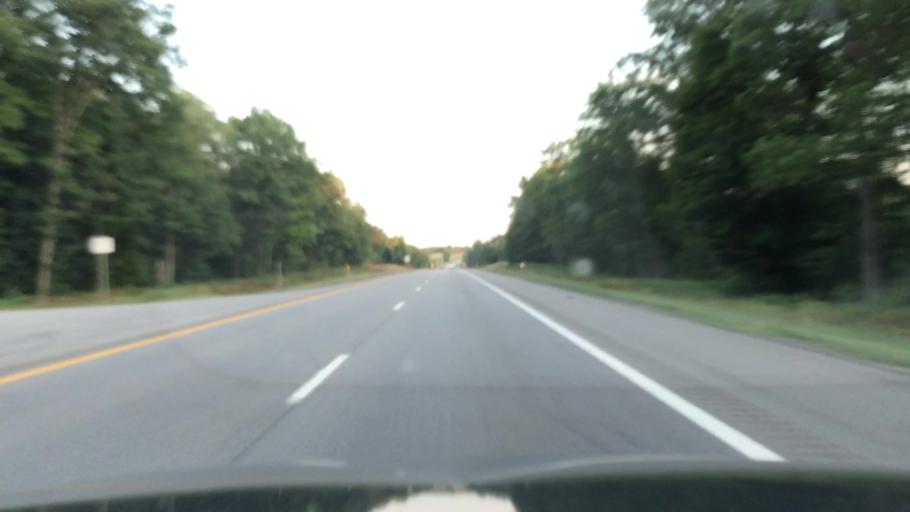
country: US
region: Michigan
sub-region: Montcalm County
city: Howard City
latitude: 43.4786
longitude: -85.4807
